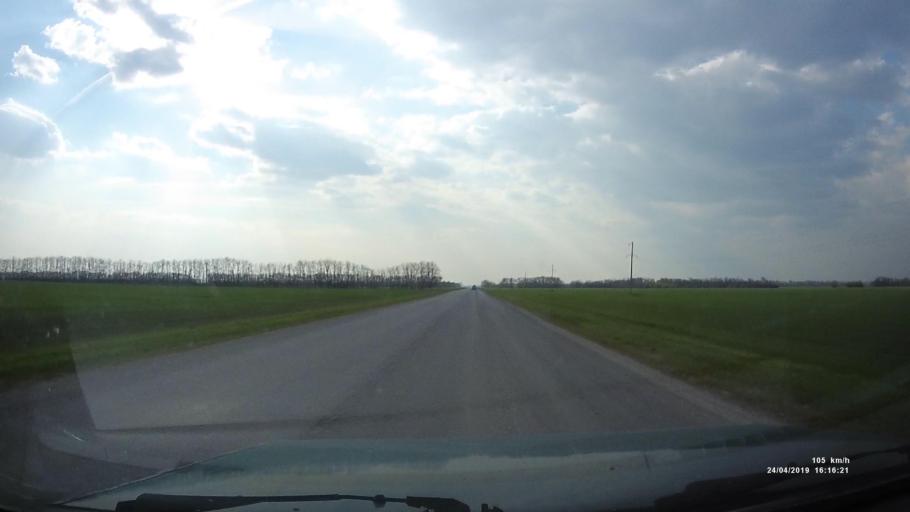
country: RU
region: Rostov
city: Sovetskoye
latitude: 46.7626
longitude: 42.1614
